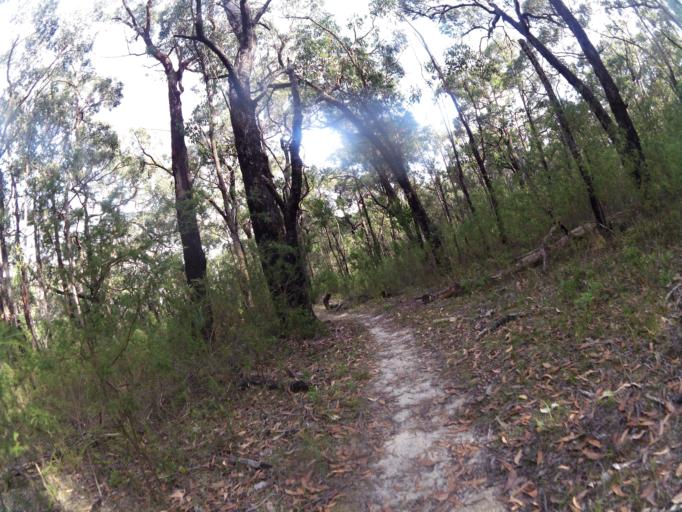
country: AU
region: Victoria
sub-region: Colac-Otway
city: Colac
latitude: -38.4901
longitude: 143.7162
